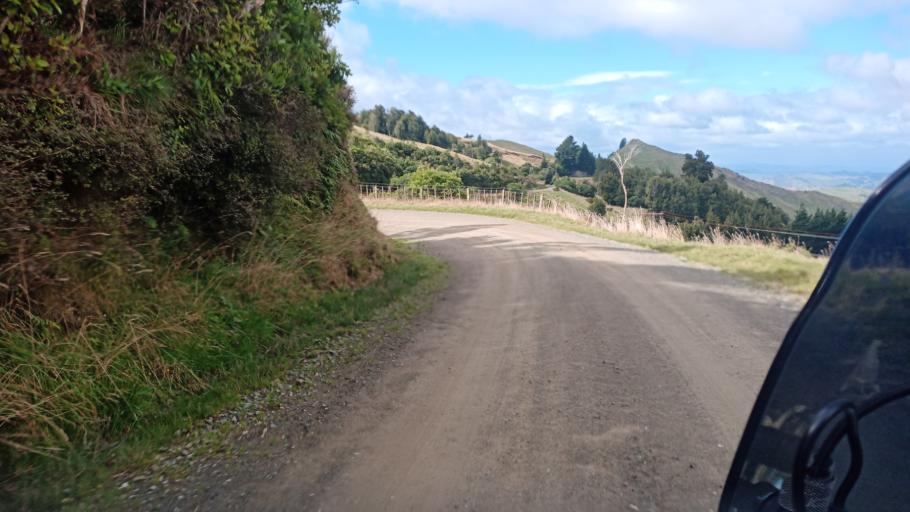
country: NZ
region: Gisborne
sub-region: Gisborne District
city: Gisborne
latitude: -38.4848
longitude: 177.5979
